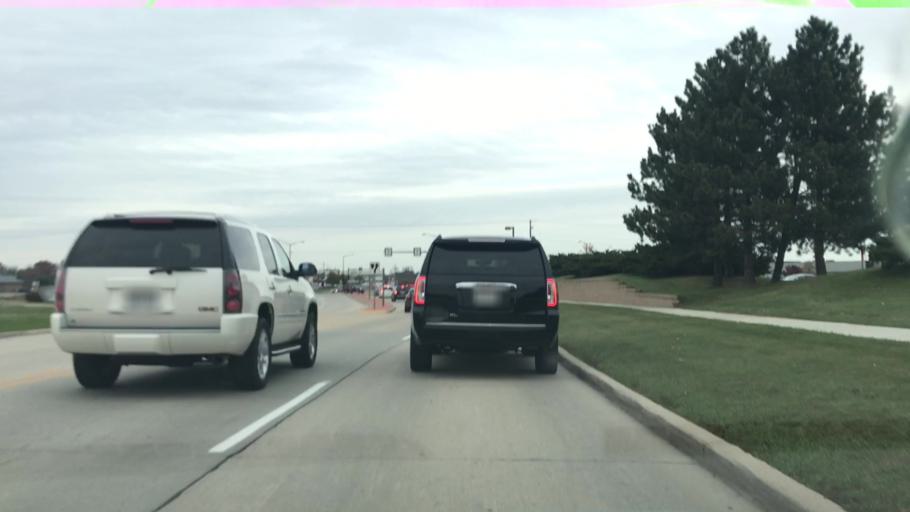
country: US
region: Wisconsin
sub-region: Brown County
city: De Pere
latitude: 44.4291
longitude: -88.1067
